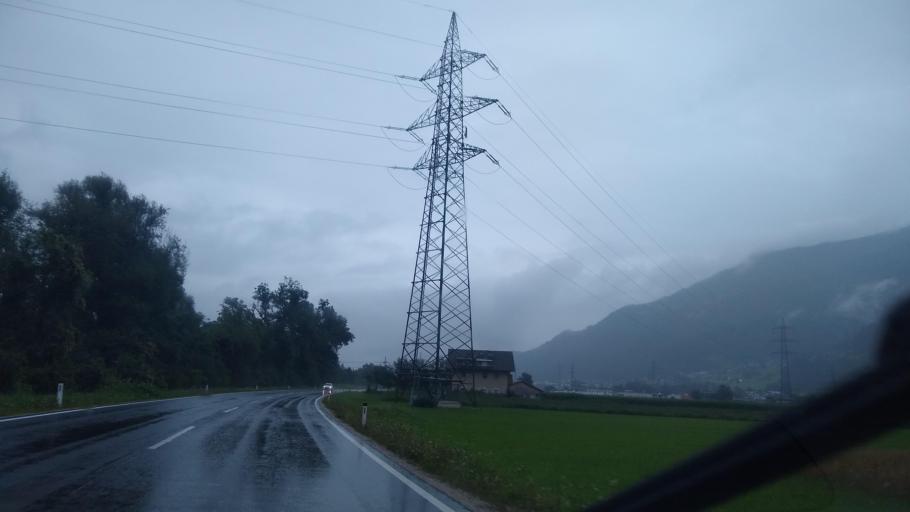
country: AT
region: Tyrol
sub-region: Politischer Bezirk Schwaz
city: Buch bei Jenbach
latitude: 47.3825
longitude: 11.7592
